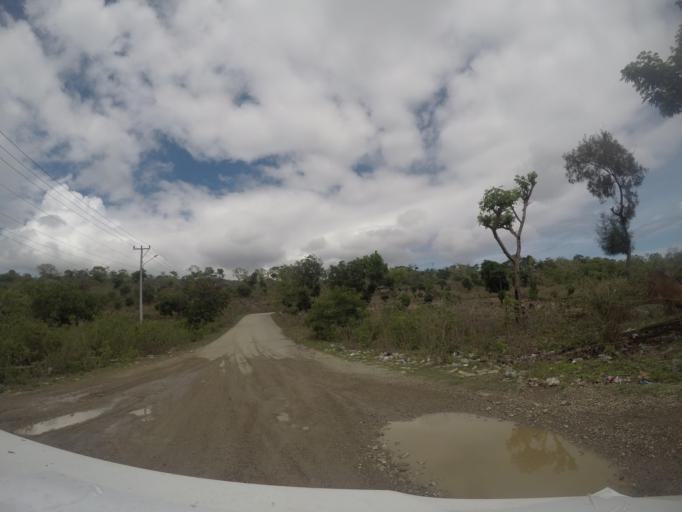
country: TL
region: Baucau
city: Baucau
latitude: -8.4699
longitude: 126.4350
